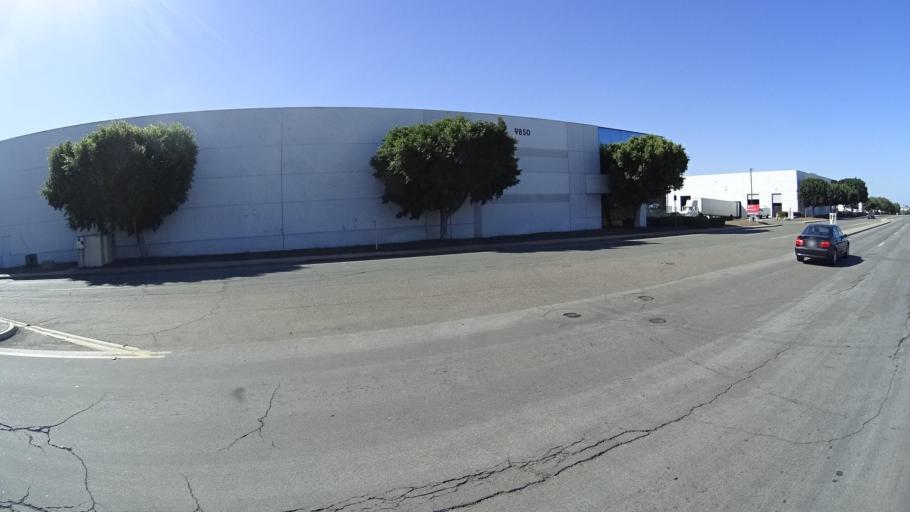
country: MX
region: Baja California
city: Tijuana
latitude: 32.5603
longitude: -116.9341
